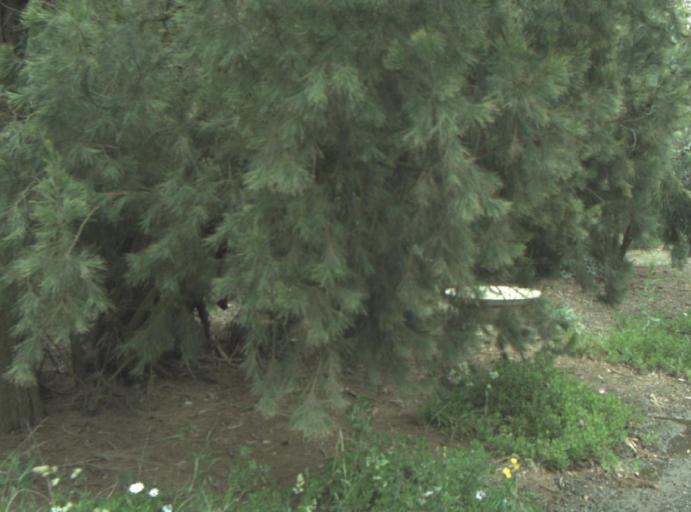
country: AU
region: Victoria
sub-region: Greater Geelong
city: Clifton Springs
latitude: -38.2009
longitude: 144.5654
